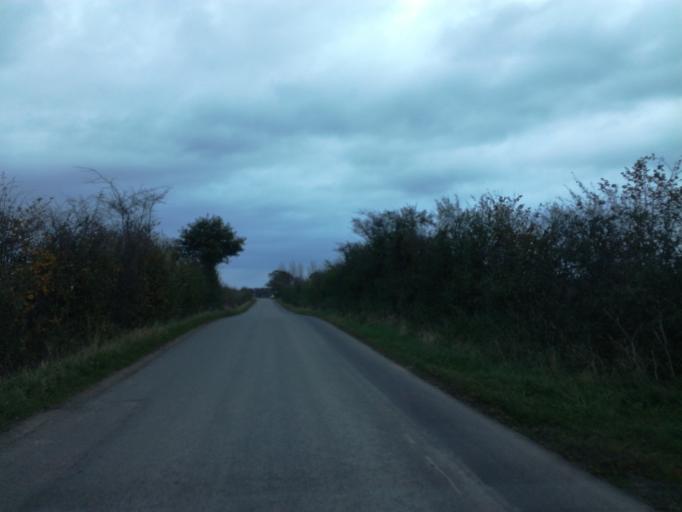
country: DK
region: South Denmark
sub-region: Fredericia Kommune
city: Fredericia
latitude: 55.6136
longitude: 9.7854
